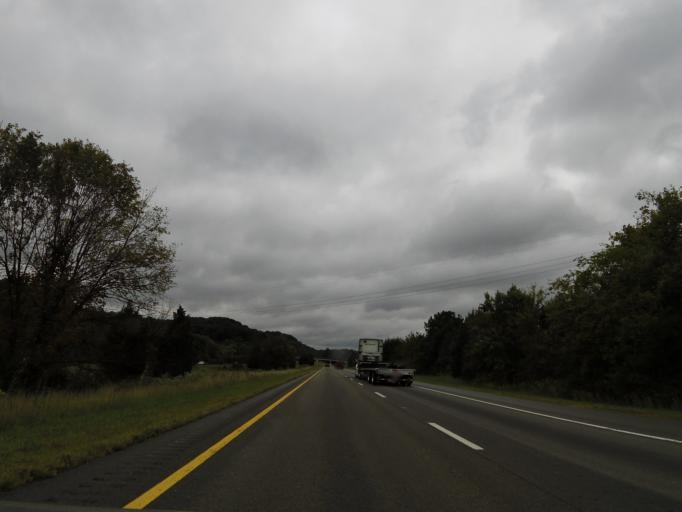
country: US
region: Tennessee
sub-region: Loudon County
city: Loudon
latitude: 35.7685
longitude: -84.3600
